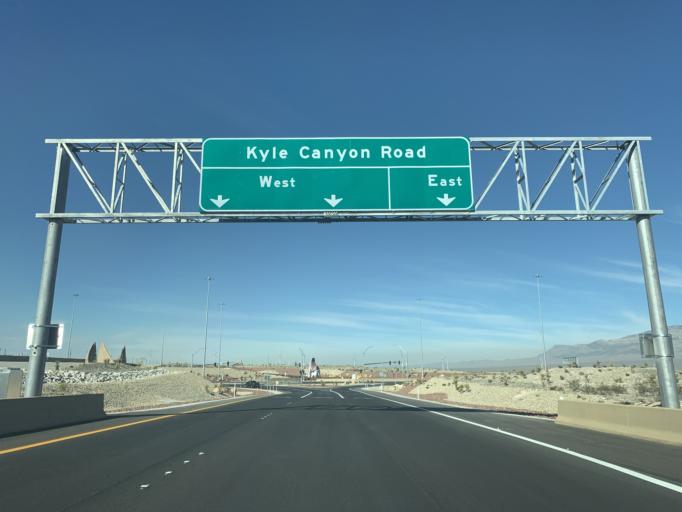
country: US
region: Nevada
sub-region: Clark County
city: Summerlin South
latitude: 36.3249
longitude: -115.3093
